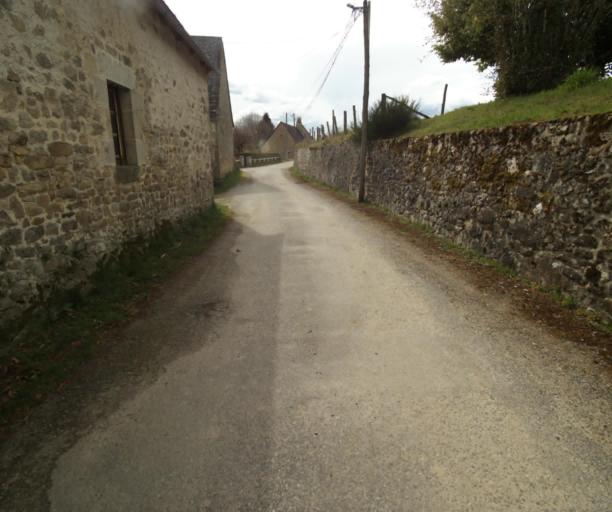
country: FR
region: Limousin
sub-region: Departement de la Correze
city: Argentat
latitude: 45.1790
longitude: 1.9436
